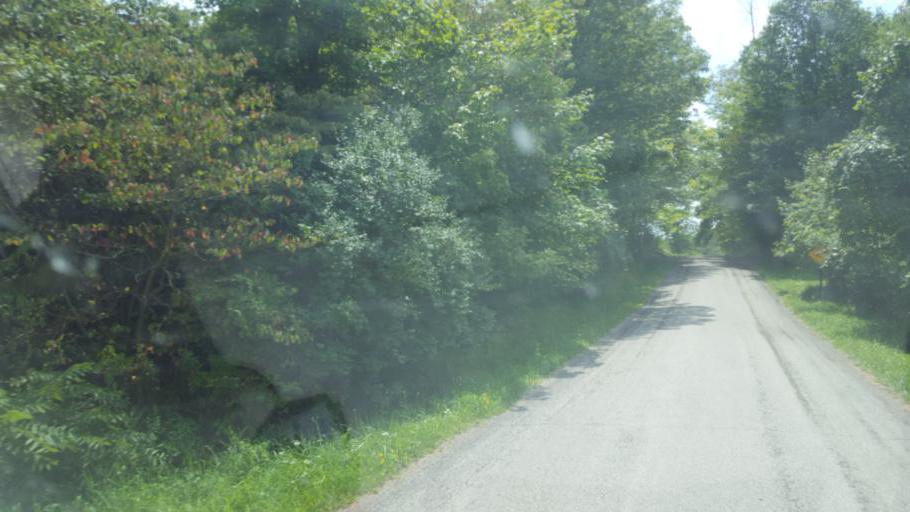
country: US
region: Ohio
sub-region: Knox County
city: Centerburg
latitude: 40.3666
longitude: -82.6341
